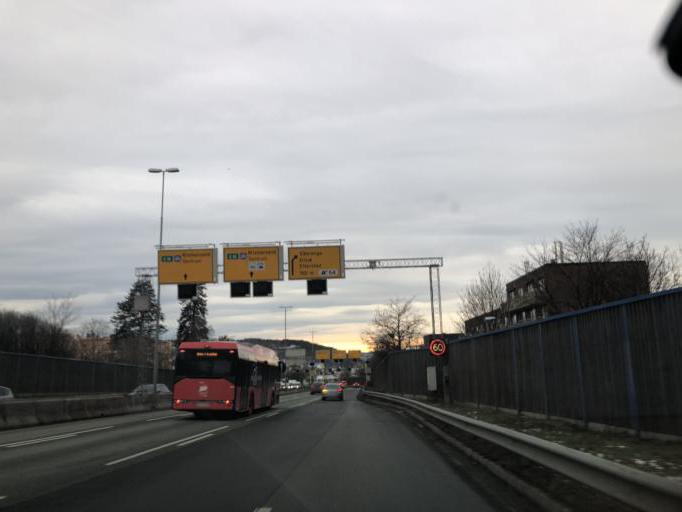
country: NO
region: Oslo
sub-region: Oslo
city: Oslo
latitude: 59.9121
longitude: 10.7970
